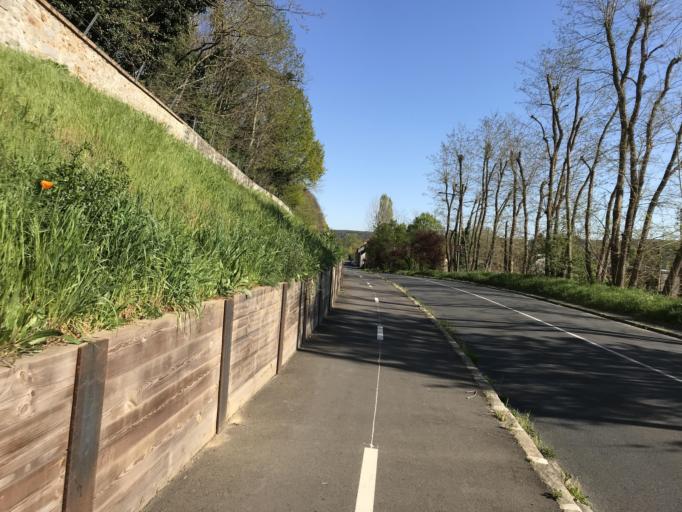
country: FR
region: Ile-de-France
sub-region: Departement de l'Essonne
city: Marcoussis
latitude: 48.6496
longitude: 2.2165
